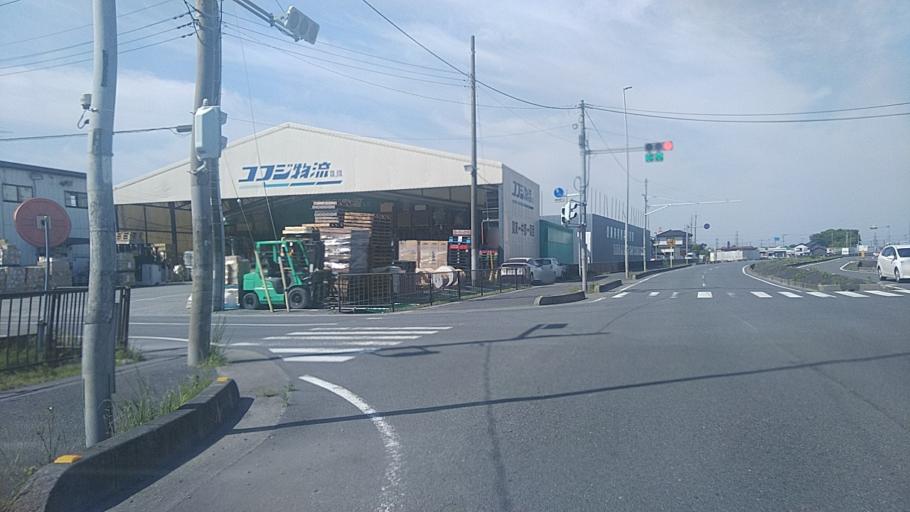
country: JP
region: Saitama
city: Koshigaya
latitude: 35.8982
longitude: 139.7632
